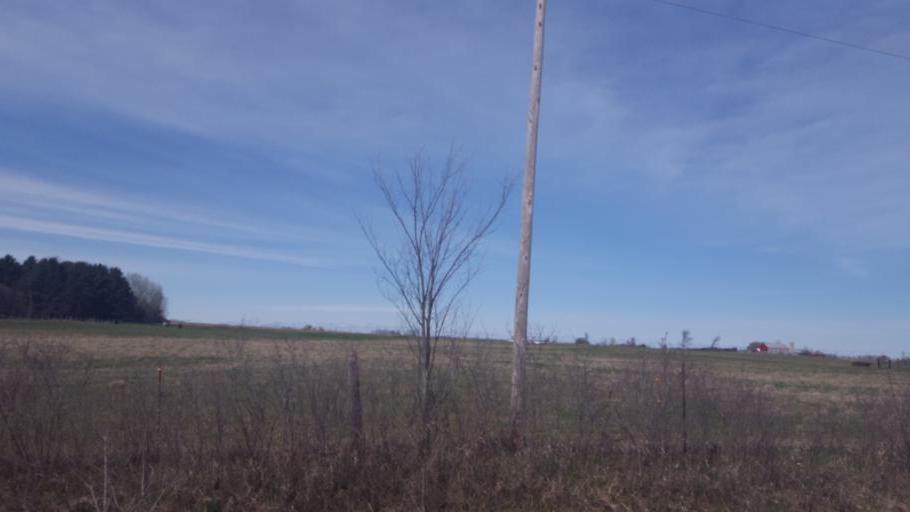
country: US
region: Michigan
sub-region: Gladwin County
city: Gladwin
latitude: 44.0599
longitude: -84.4752
